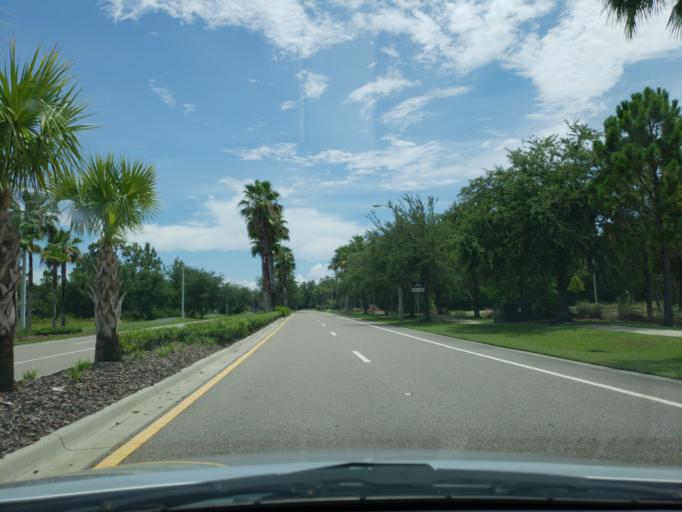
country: US
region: Florida
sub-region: Hillsborough County
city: Pebble Creek
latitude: 28.1295
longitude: -82.3823
